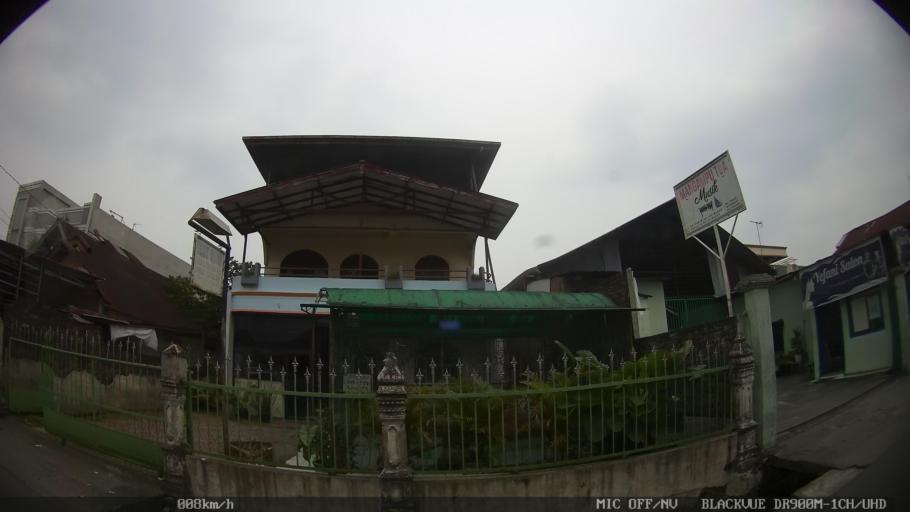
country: ID
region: North Sumatra
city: Medan
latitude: 3.5671
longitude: 98.7027
